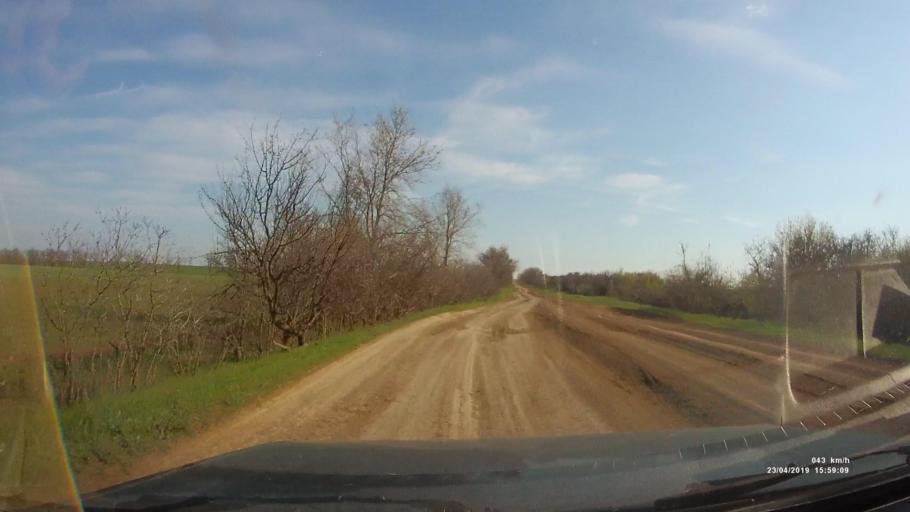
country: RU
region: Rostov
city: Remontnoye
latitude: 46.5188
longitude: 43.1096
